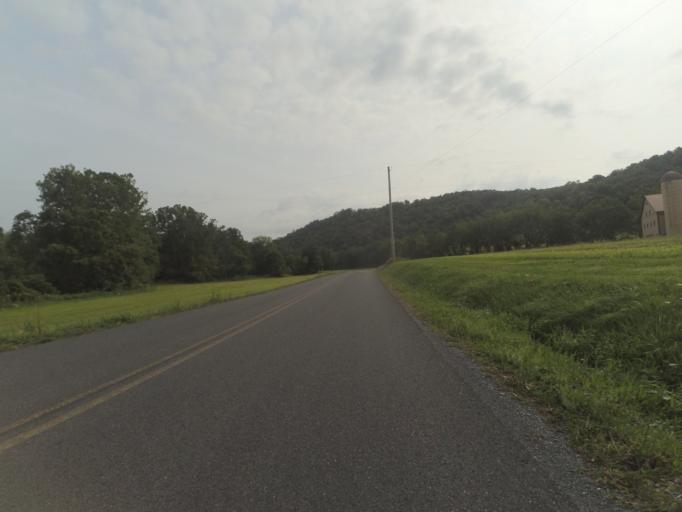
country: US
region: Pennsylvania
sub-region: Huntingdon County
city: Huntingdon
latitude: 40.5377
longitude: -78.0752
